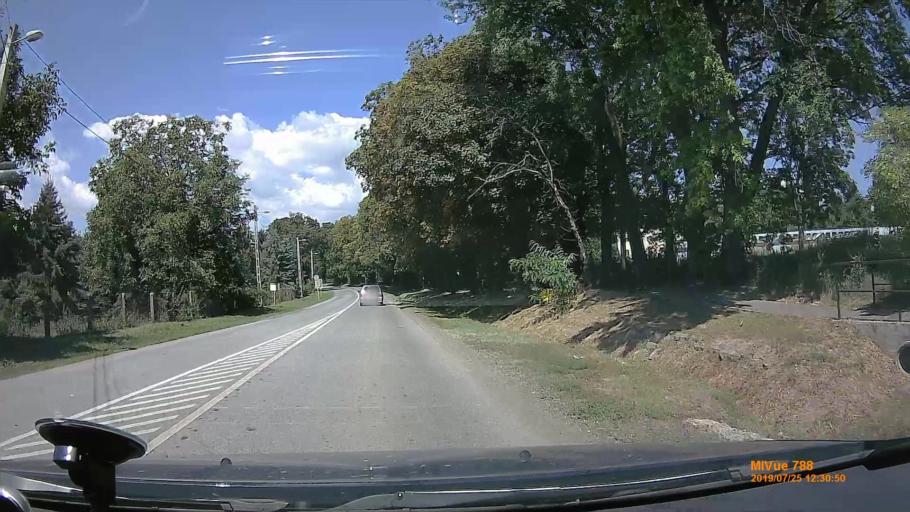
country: HU
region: Borsod-Abauj-Zemplen
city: Tarcal
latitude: 48.1412
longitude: 21.3360
